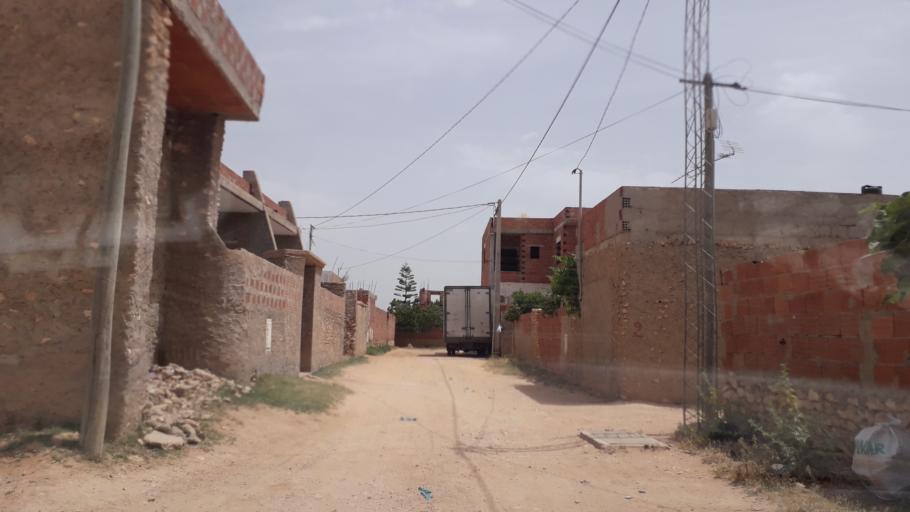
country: TN
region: Safaqis
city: Al Qarmadah
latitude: 34.8433
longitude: 10.7748
